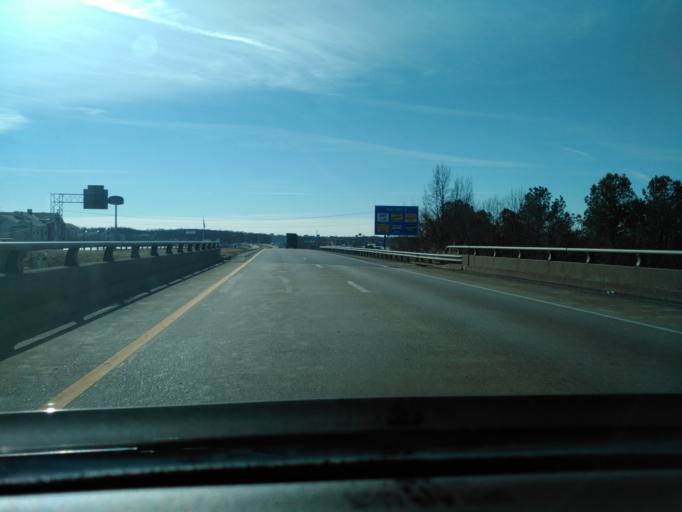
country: US
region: Kentucky
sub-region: McCracken County
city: Hendron
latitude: 37.0871
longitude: -88.6845
